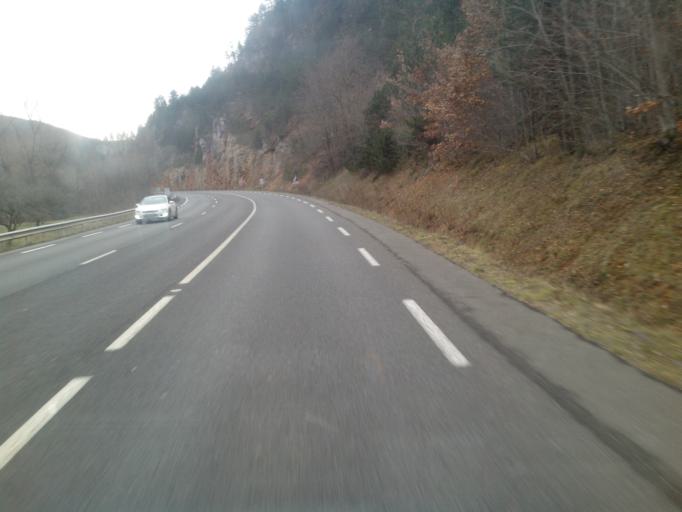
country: FR
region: Languedoc-Roussillon
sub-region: Departement de la Lozere
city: Mende
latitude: 44.4992
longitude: 3.4624
